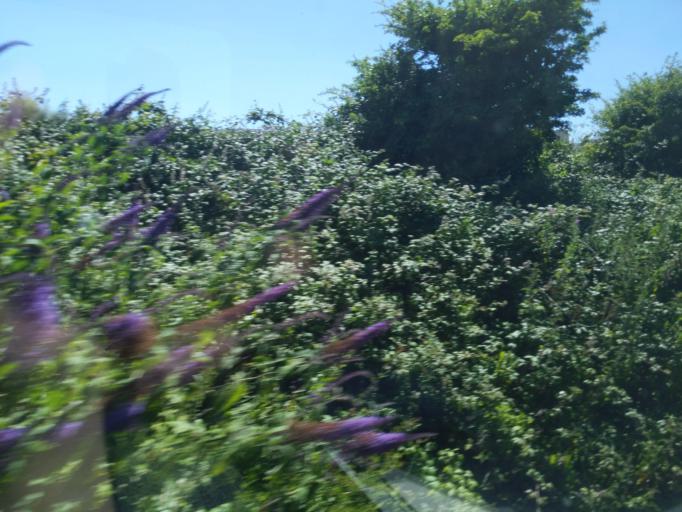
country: GB
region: England
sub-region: Cornwall
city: Hayle
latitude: 50.1906
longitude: -5.4011
